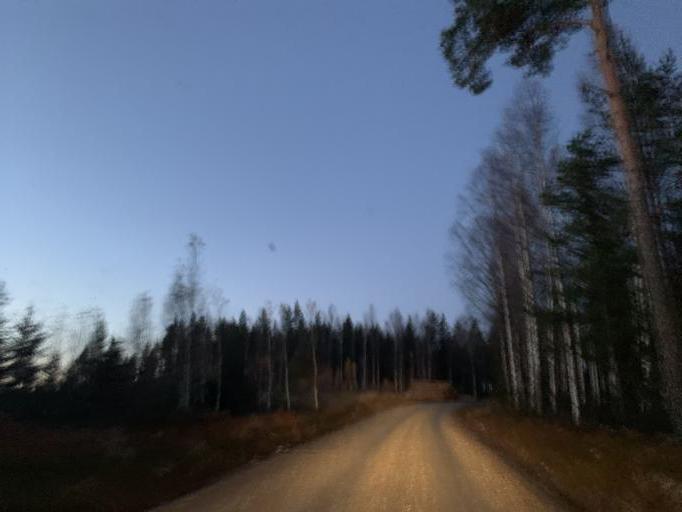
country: SE
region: OErebro
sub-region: Lindesbergs Kommun
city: Fellingsbro
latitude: 59.3795
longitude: 15.6670
